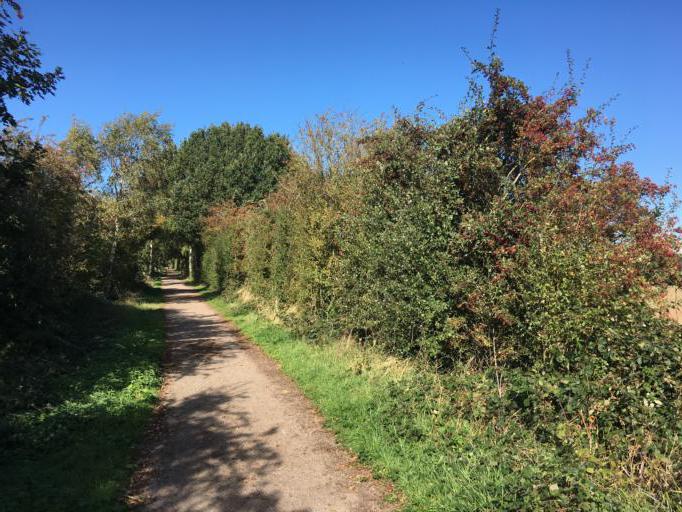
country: GB
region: England
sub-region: Warwickshire
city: Kenilworth
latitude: 52.3687
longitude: -1.5861
